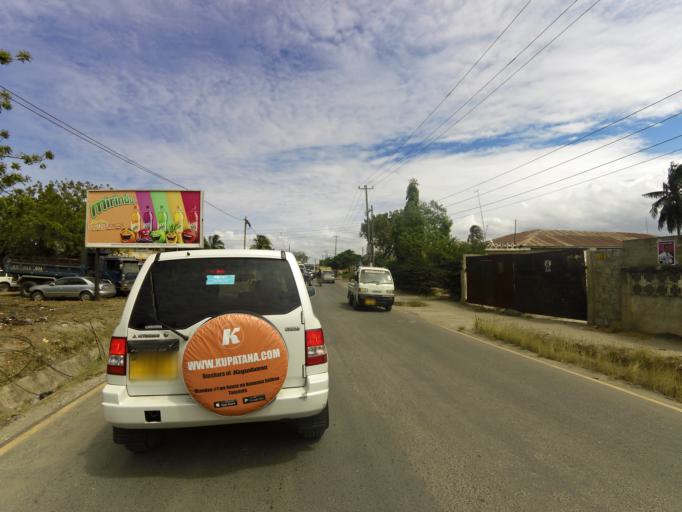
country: TZ
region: Dar es Salaam
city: Magomeni
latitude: -6.8064
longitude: 39.2513
